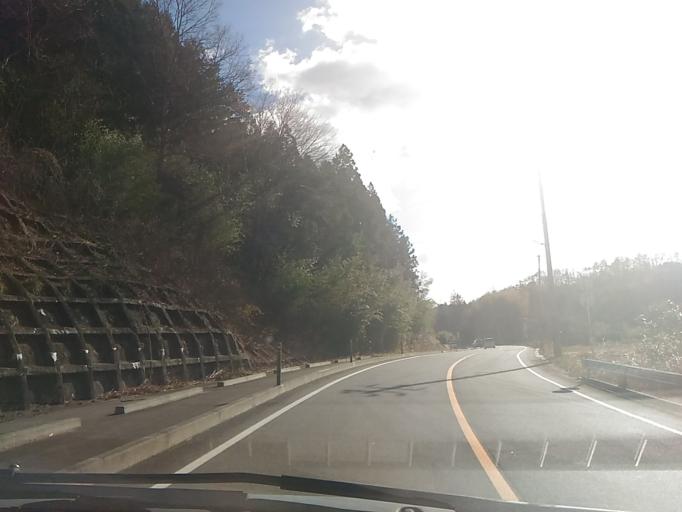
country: JP
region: Fukushima
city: Iwaki
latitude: 37.0135
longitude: 140.7733
